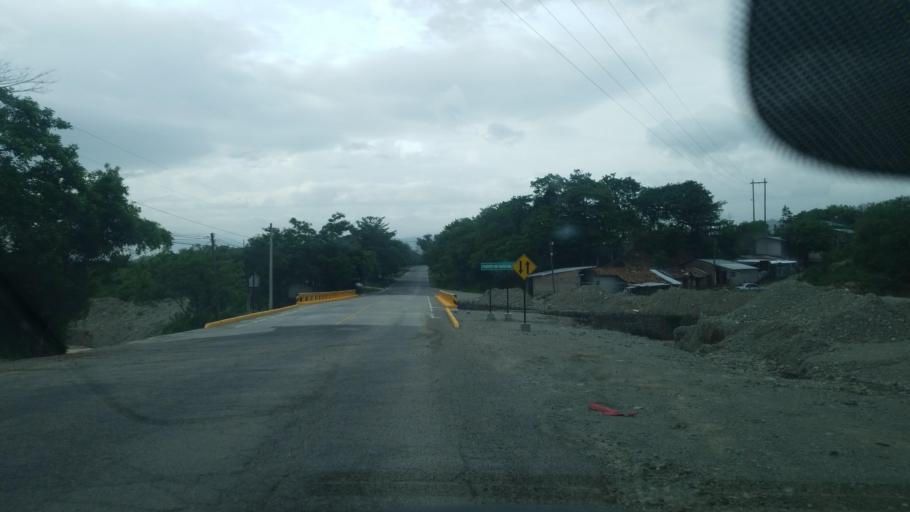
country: HN
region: Ocotepeque
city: Santa Lucia
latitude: 14.4127
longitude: -89.1947
